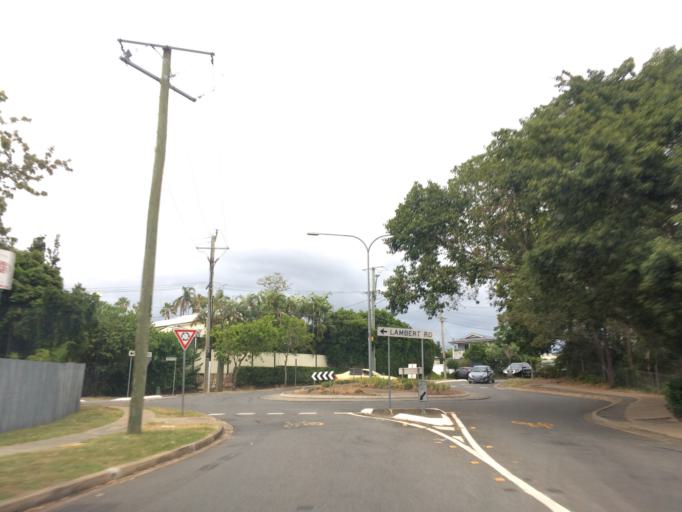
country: AU
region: Queensland
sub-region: Brisbane
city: Taringa
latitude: -27.5036
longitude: 152.9806
